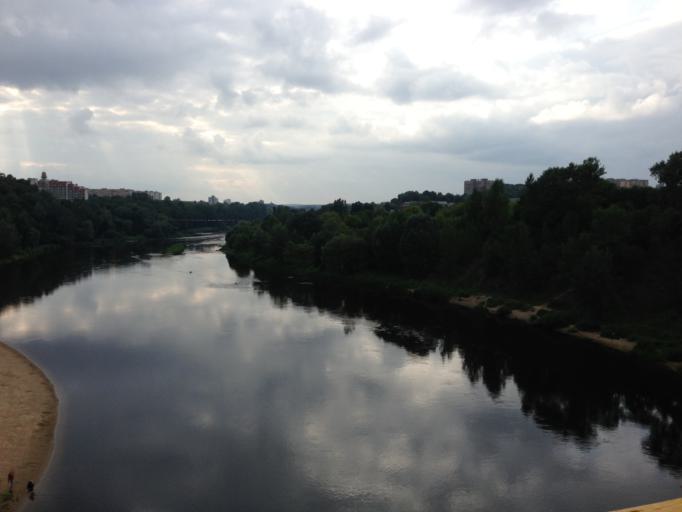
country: BY
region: Grodnenskaya
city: Hrodna
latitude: 53.6613
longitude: 23.8595
